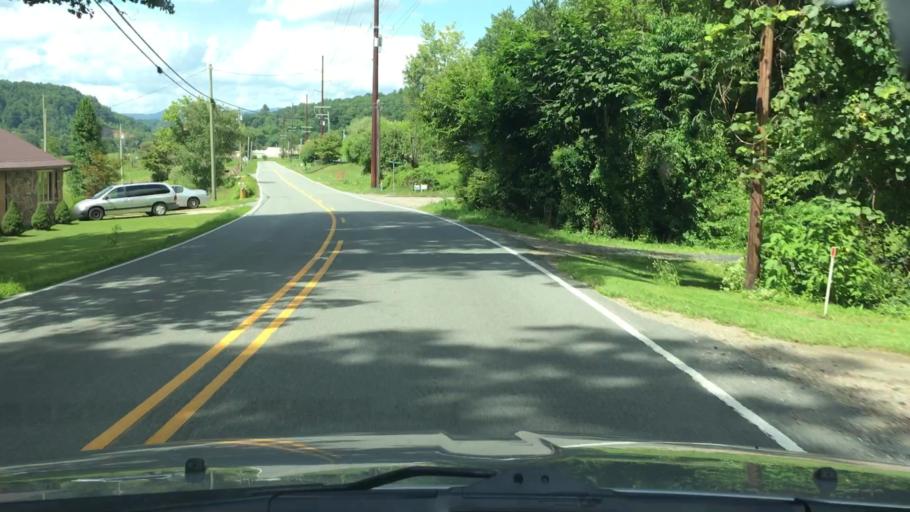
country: US
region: North Carolina
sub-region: Yancey County
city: Burnsville
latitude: 35.8851
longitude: -82.2155
